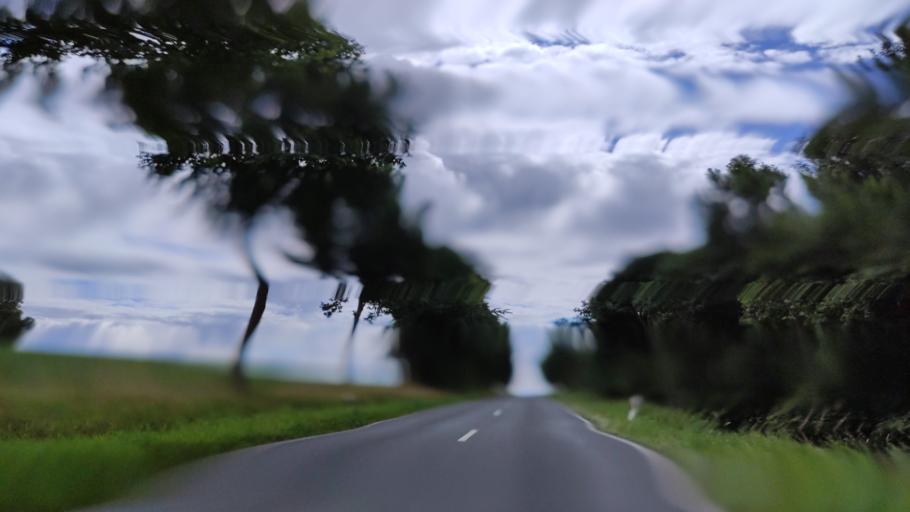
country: DE
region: North Rhine-Westphalia
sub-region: Regierungsbezirk Detmold
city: Schieder-Schwalenberg
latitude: 51.8057
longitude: 9.1934
